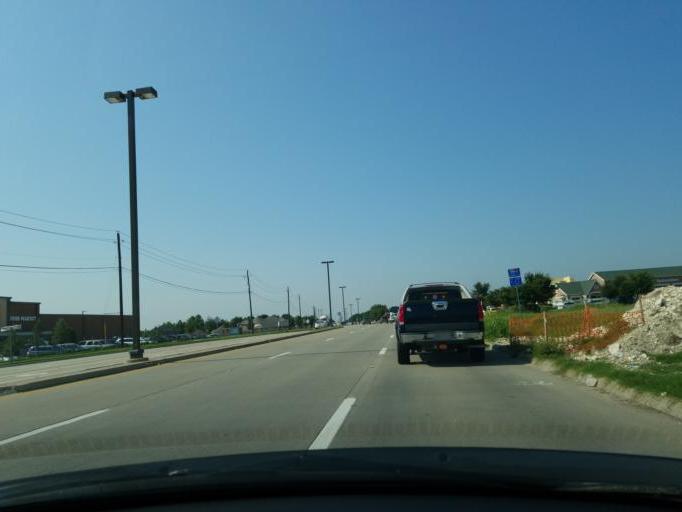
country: US
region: Texas
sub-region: Collin County
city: Fairview
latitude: 33.1291
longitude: -96.6453
